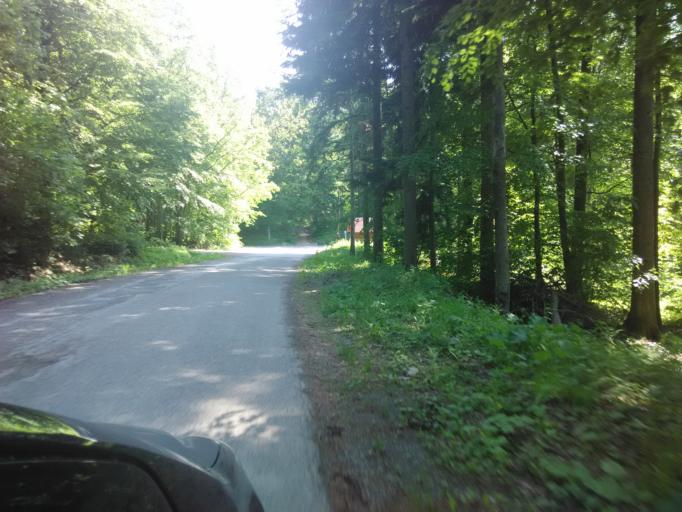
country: SK
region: Banskobystricky
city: Revuca
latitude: 48.6499
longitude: 20.2964
